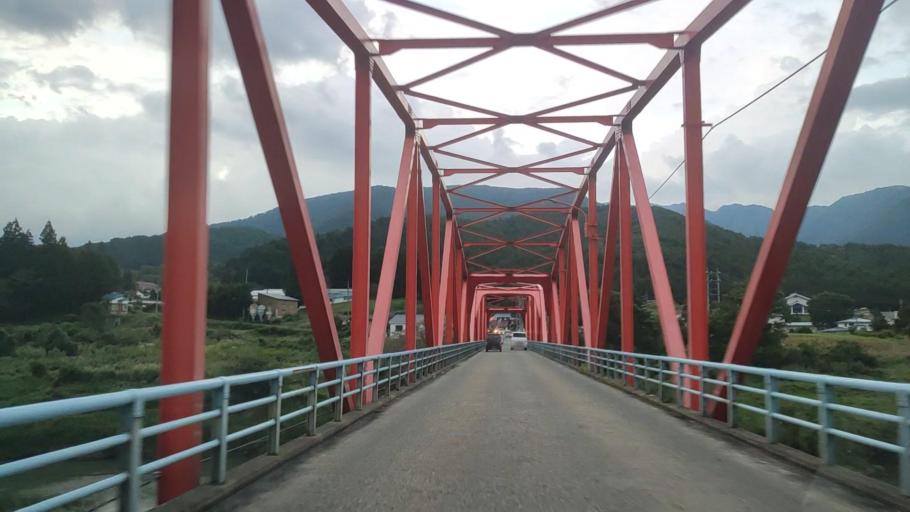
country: JP
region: Nagano
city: Iiyama
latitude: 36.8924
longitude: 138.4031
